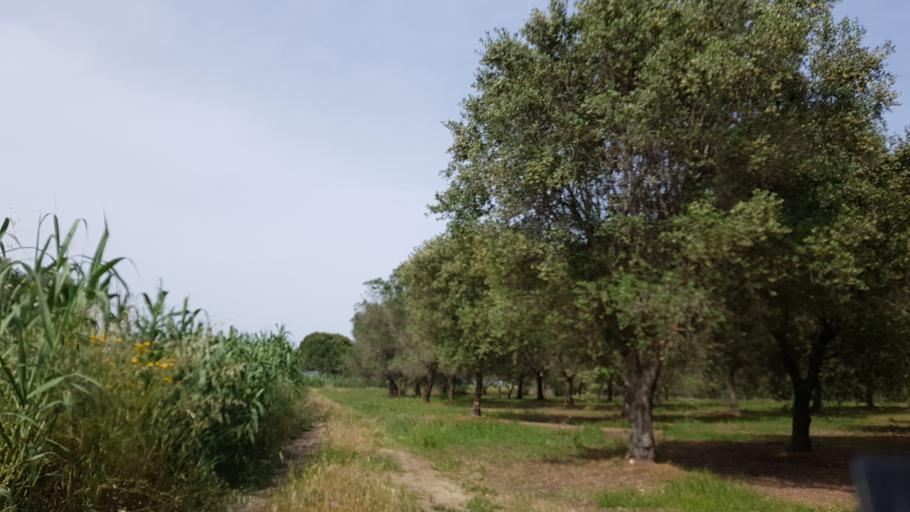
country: IT
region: Apulia
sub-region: Provincia di Brindisi
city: La Rosa
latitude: 40.5901
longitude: 18.0017
